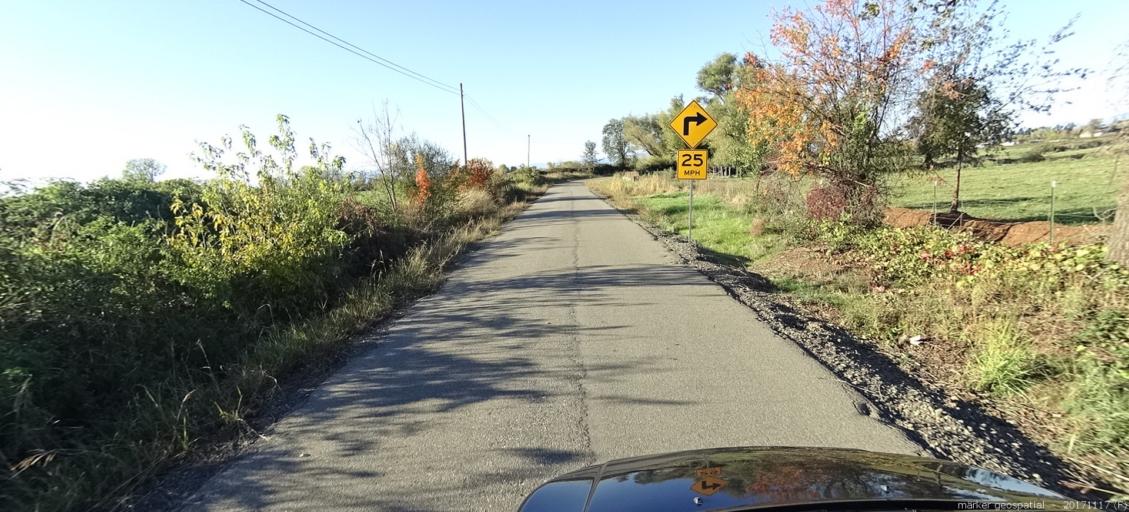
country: US
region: California
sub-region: Shasta County
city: Cottonwood
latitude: 40.4134
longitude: -122.2248
